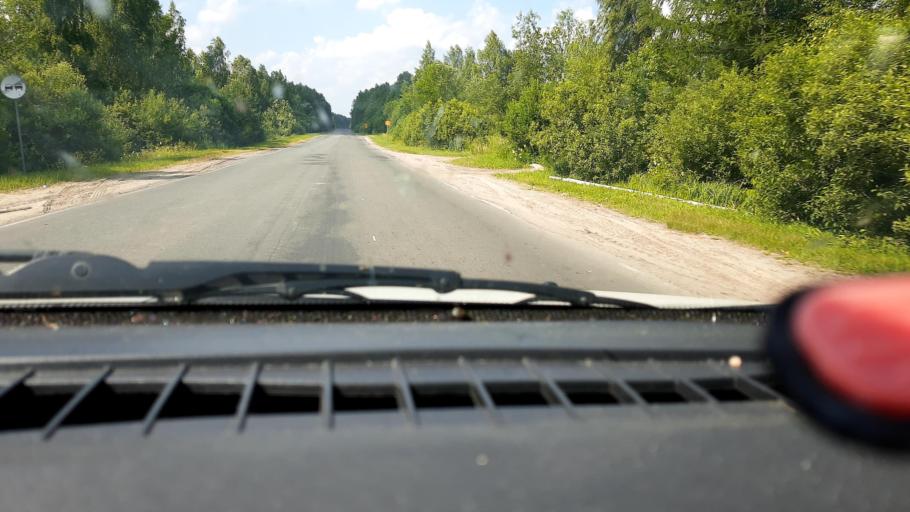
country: RU
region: Nizjnij Novgorod
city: Prudy
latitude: 57.4058
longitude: 46.0768
